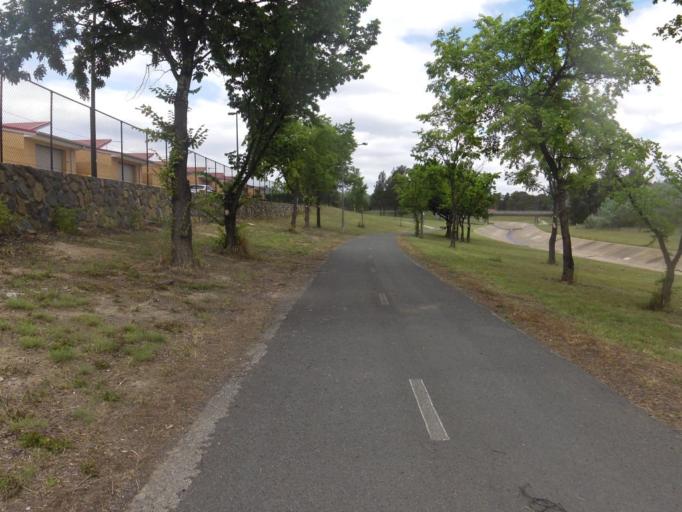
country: AU
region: Australian Capital Territory
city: Macarthur
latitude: -35.4205
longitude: 149.0934
